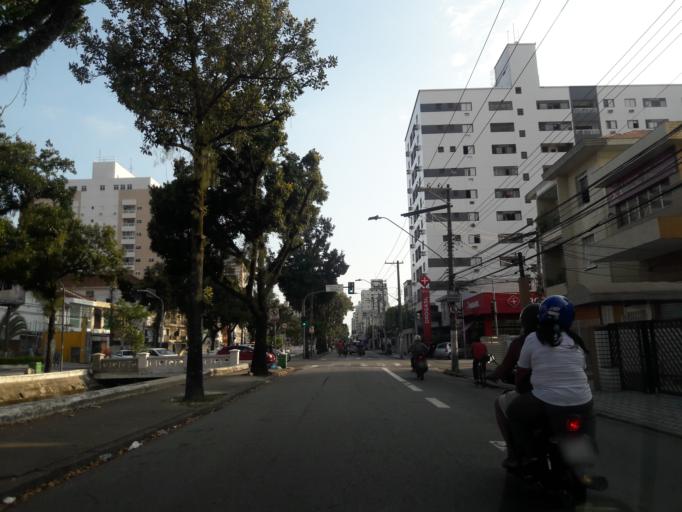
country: BR
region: Sao Paulo
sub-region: Santos
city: Santos
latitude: -23.9589
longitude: -46.3381
